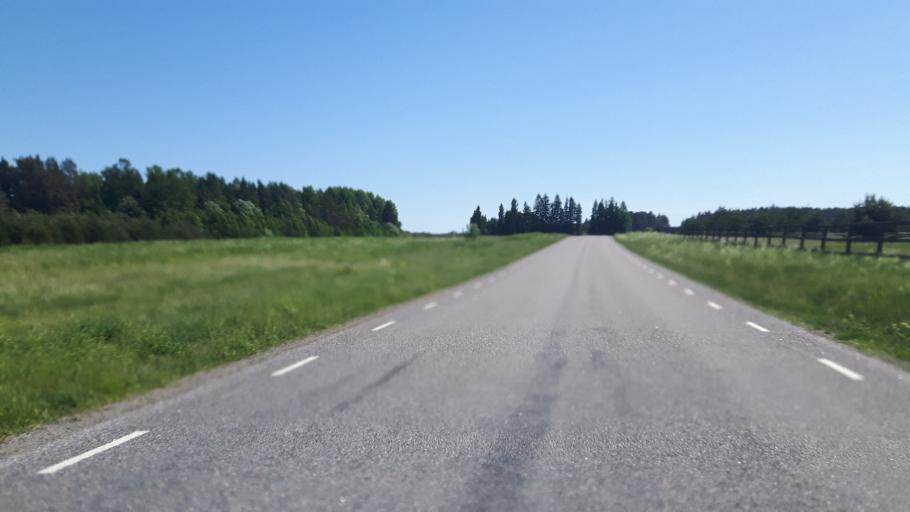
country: EE
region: Raplamaa
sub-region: Kohila vald
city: Kohila
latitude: 59.1985
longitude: 24.6952
